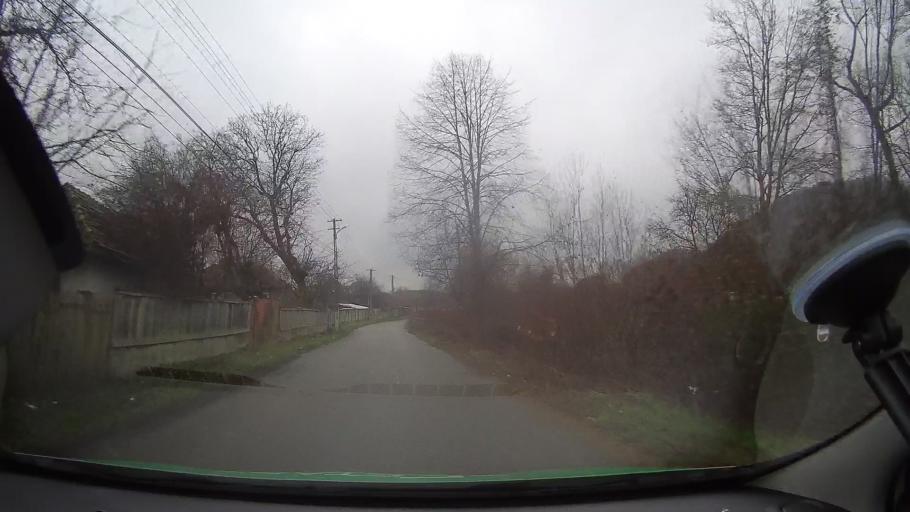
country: RO
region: Arad
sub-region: Comuna Halmagel
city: Halmagel
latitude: 46.2675
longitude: 22.6232
